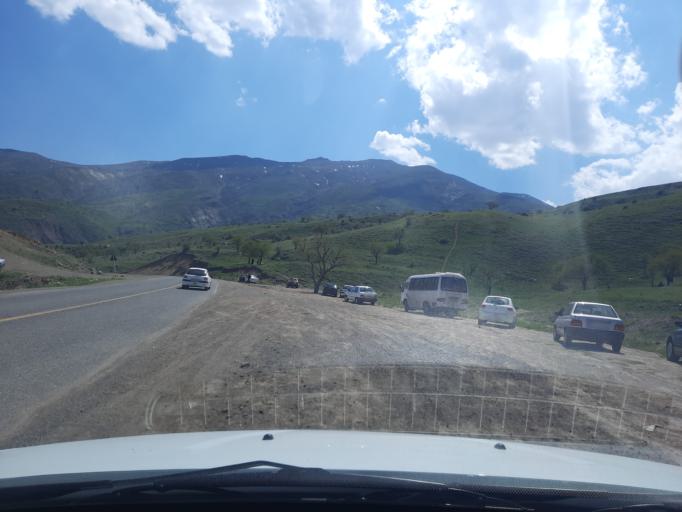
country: IR
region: Qazvin
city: Qazvin
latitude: 36.4106
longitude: 50.2442
